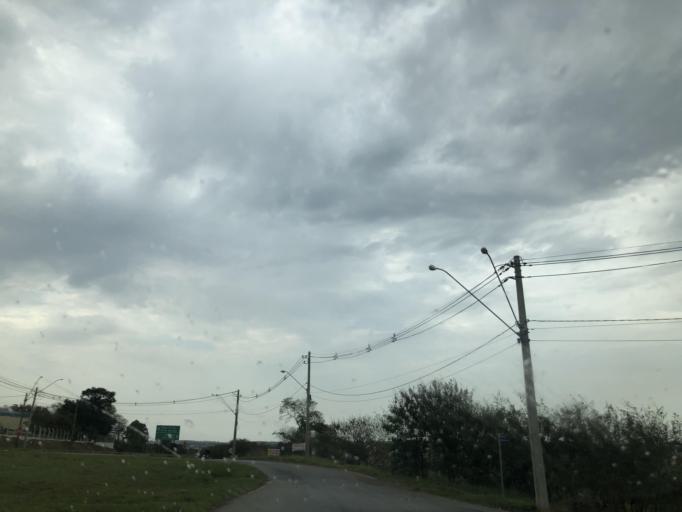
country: BR
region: Sao Paulo
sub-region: Salto De Pirapora
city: Salto de Pirapora
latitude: -23.6568
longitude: -47.5874
